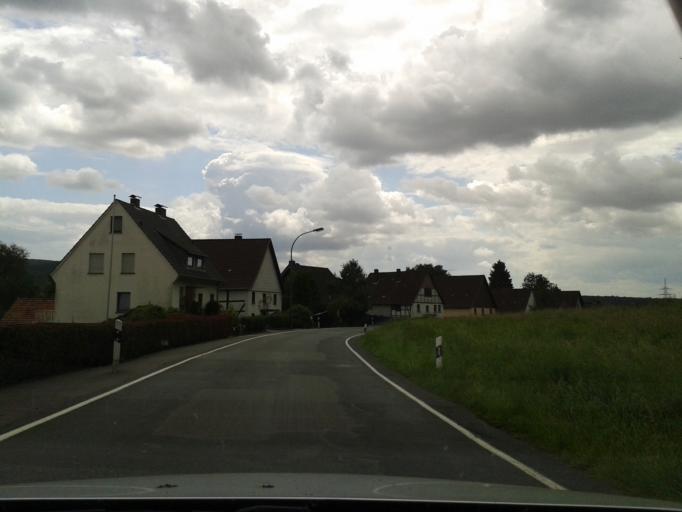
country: DE
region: North Rhine-Westphalia
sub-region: Regierungsbezirk Detmold
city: Blomberg
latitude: 51.9312
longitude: 9.1525
